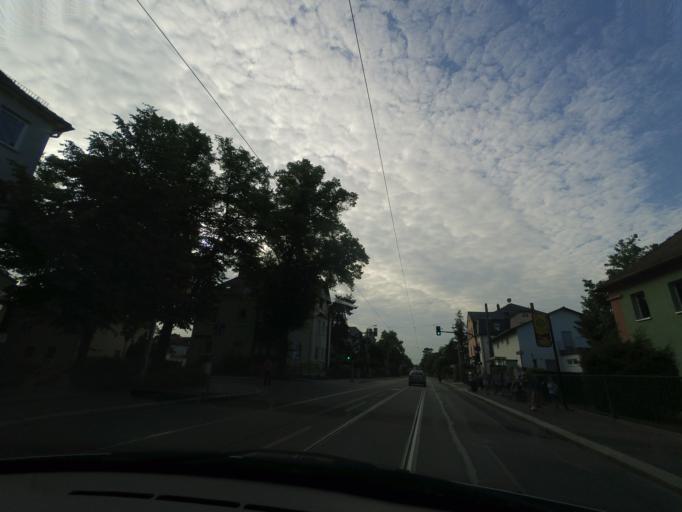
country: DE
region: Saxony
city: Heidenau
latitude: 51.0277
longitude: 13.8349
